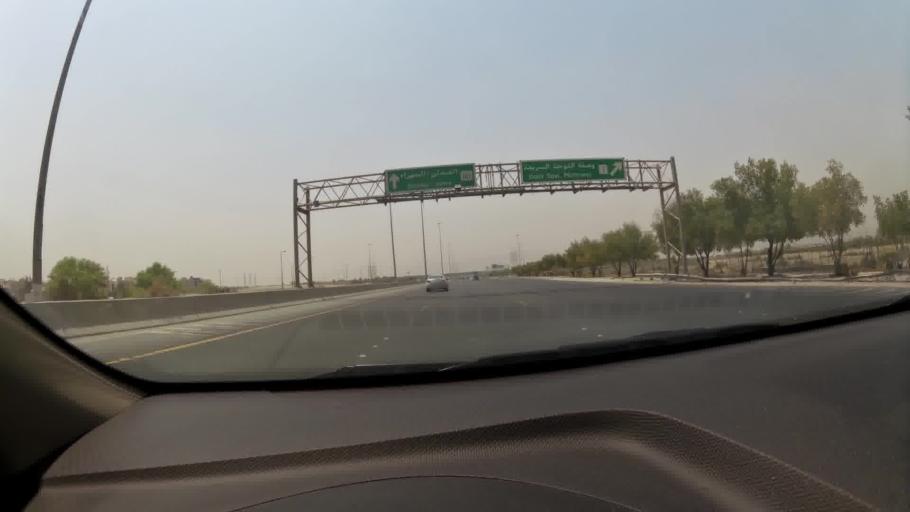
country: KW
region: Muhafazat al Jahra'
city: Al Jahra'
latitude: 29.3117
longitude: 47.7933
